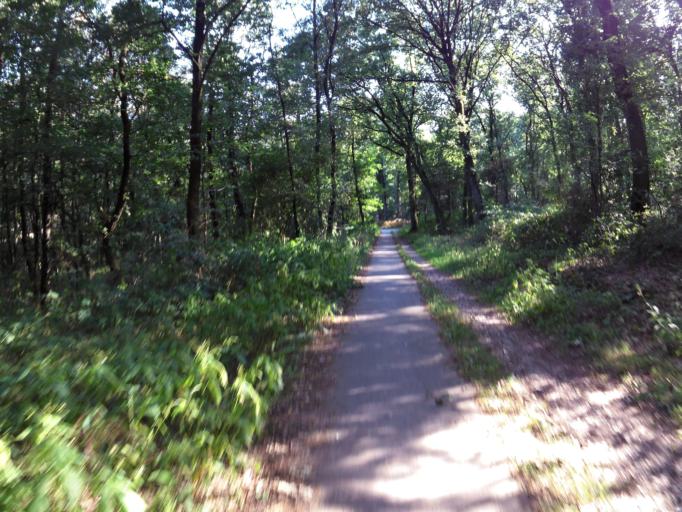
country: NL
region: Gelderland
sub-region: Gemeente Montferland
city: s-Heerenberg
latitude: 51.8777
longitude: 6.1997
